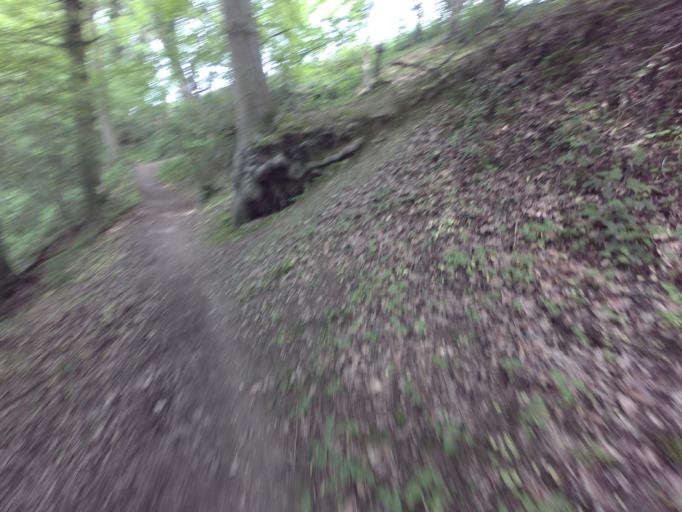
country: BE
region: Wallonia
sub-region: Province de Liege
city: Plombieres
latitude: 50.7614
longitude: 5.9325
